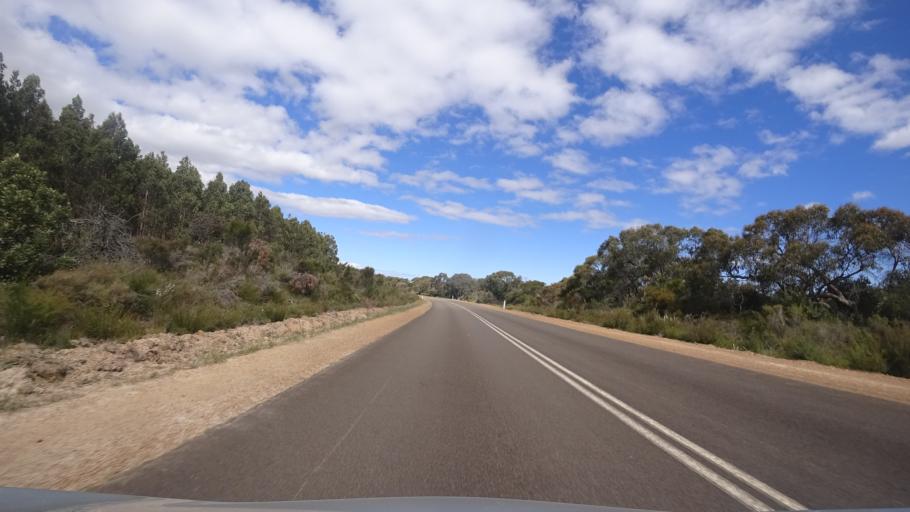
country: AU
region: South Australia
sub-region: Kangaroo Island
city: Kingscote
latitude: -35.8024
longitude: 137.0552
